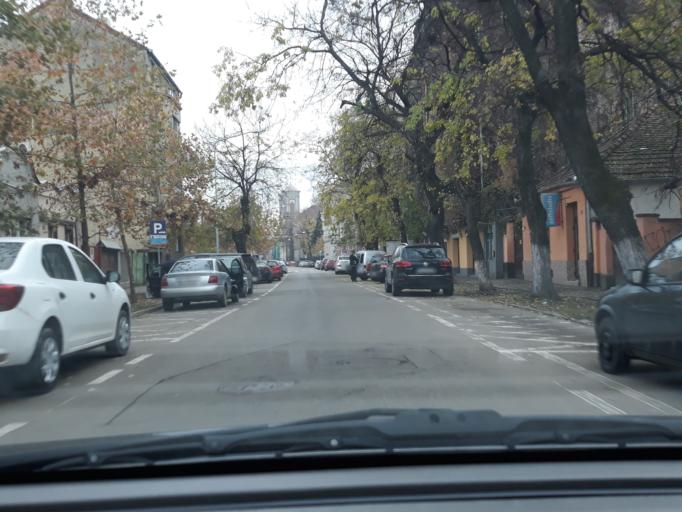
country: RO
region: Bihor
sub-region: Comuna Biharea
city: Oradea
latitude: 47.0625
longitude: 21.9295
